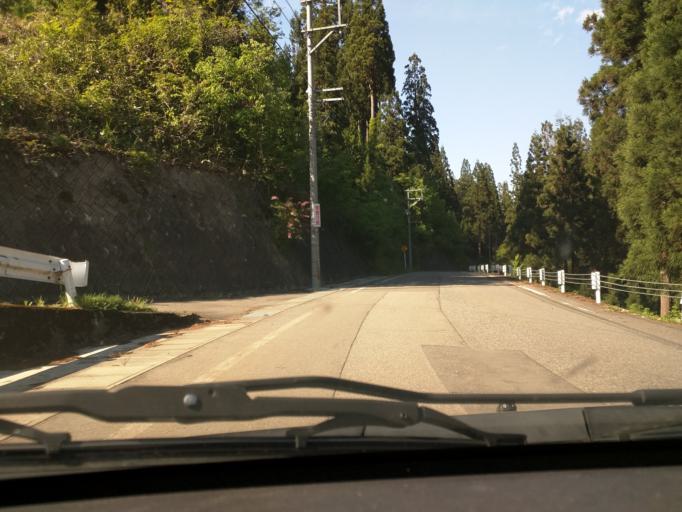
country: JP
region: Fukushima
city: Kitakata
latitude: 37.5577
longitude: 139.6246
